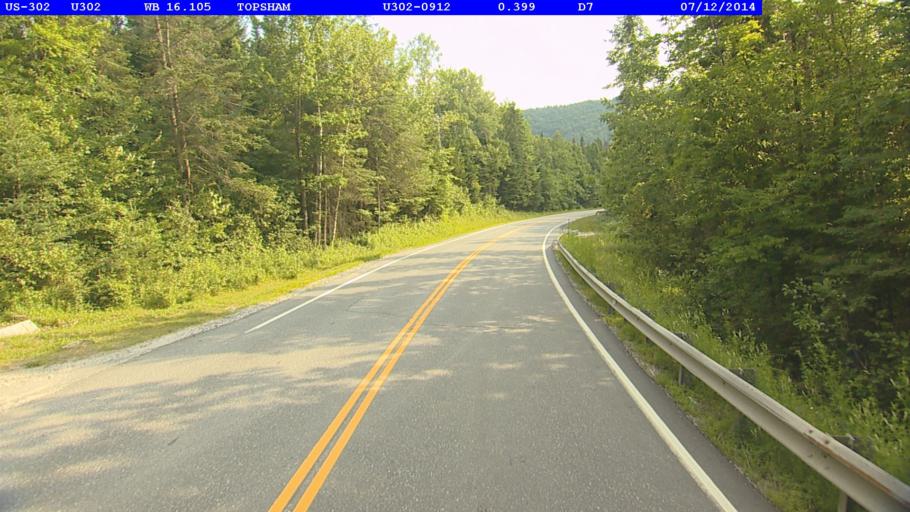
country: US
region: Vermont
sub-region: Washington County
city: South Barre
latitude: 44.1433
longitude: -72.3106
